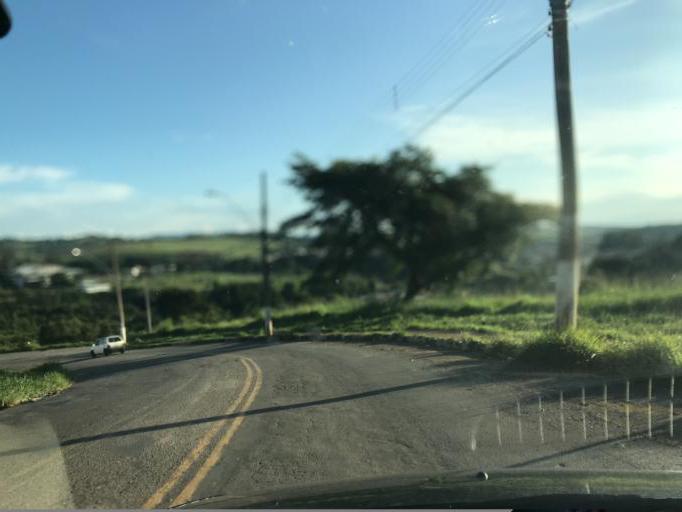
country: BR
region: Minas Gerais
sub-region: Tres Coracoes
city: Tres Coracoes
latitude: -21.6956
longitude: -45.2453
